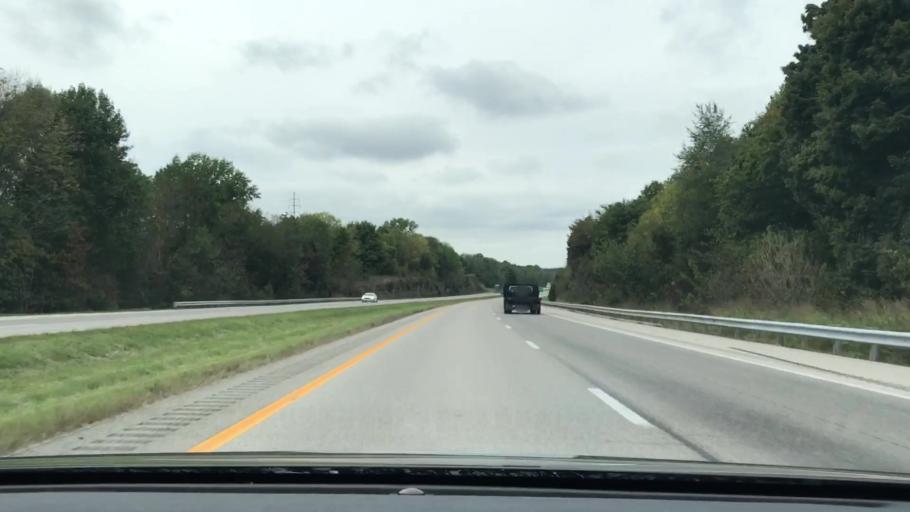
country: US
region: Kentucky
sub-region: Barren County
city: Glasgow
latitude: 36.9738
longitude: -85.9242
